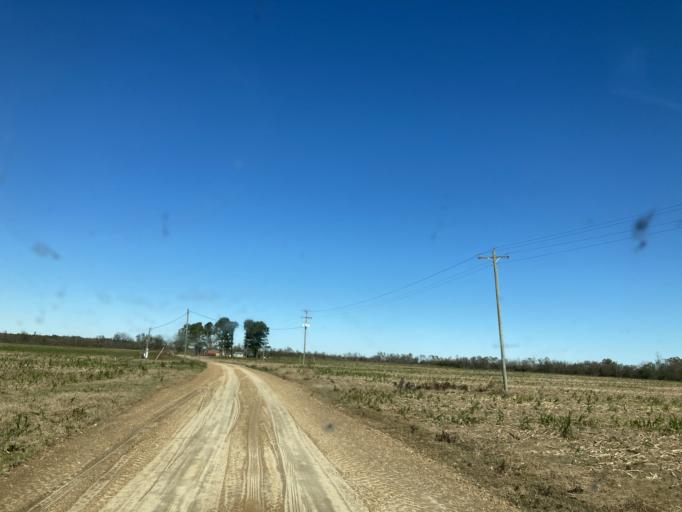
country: US
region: Mississippi
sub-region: Hinds County
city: Lynchburg
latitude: 32.6269
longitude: -90.5753
